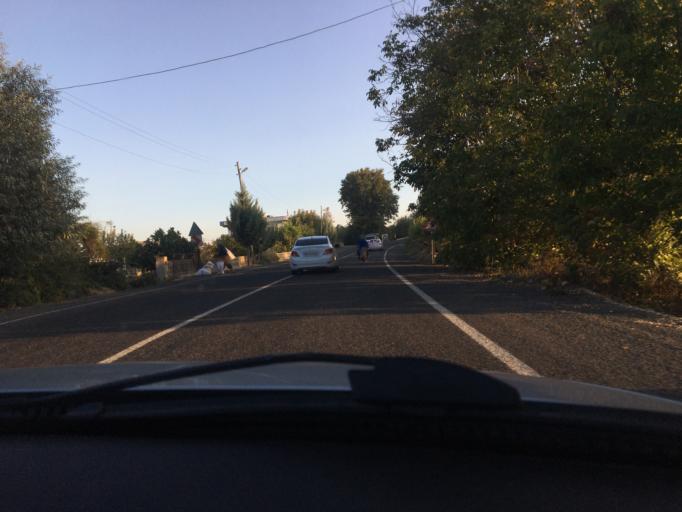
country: TR
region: Sanliurfa
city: Halfeti
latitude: 37.2073
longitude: 37.9699
